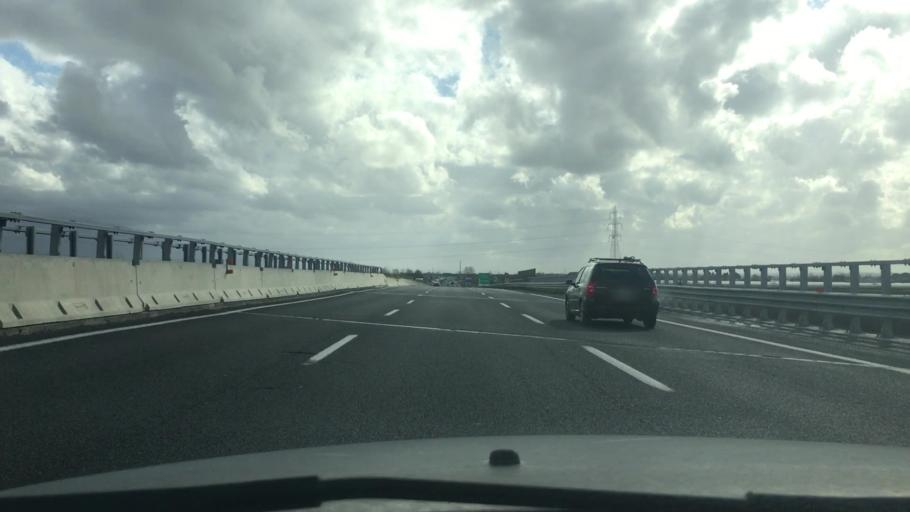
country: IT
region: Campania
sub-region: Provincia di Napoli
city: Pascarola
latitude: 40.9858
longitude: 14.3252
